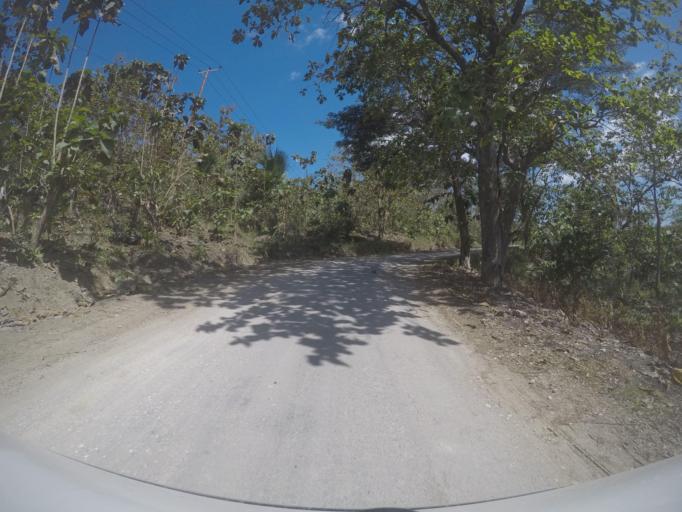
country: TL
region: Viqueque
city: Viqueque
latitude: -8.9033
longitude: 126.3929
